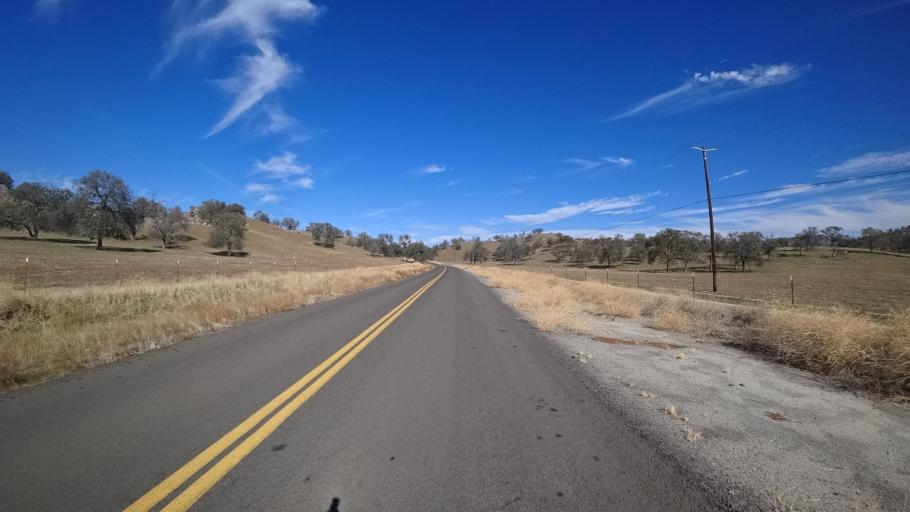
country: US
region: California
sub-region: Kern County
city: Oildale
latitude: 35.6373
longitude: -118.8380
